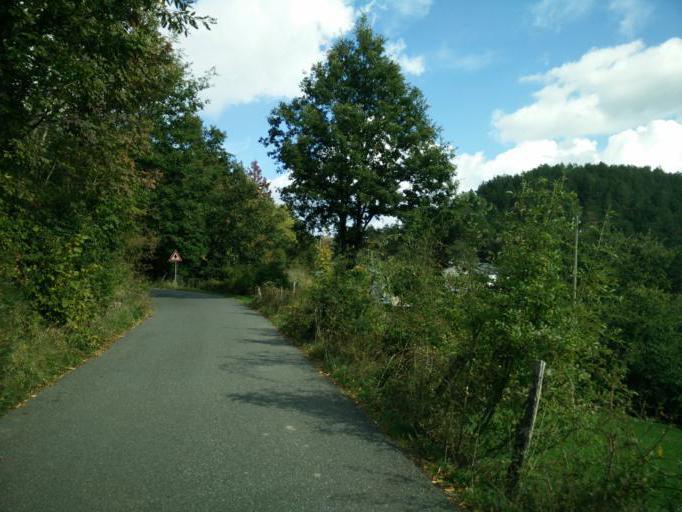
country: IT
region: Tuscany
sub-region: Provincia di Massa-Carrara
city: Patigno
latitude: 44.3536
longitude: 9.7521
